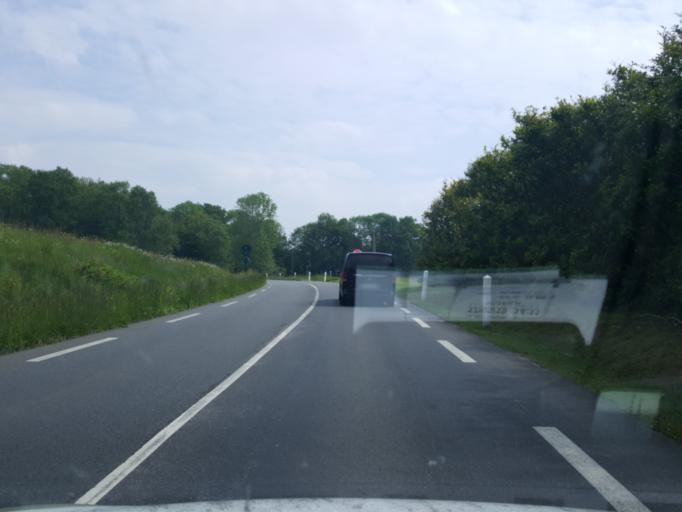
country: FR
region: Ile-de-France
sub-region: Departement du Val-d'Oise
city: Magny-en-Vexin
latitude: 49.0858
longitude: 1.7860
